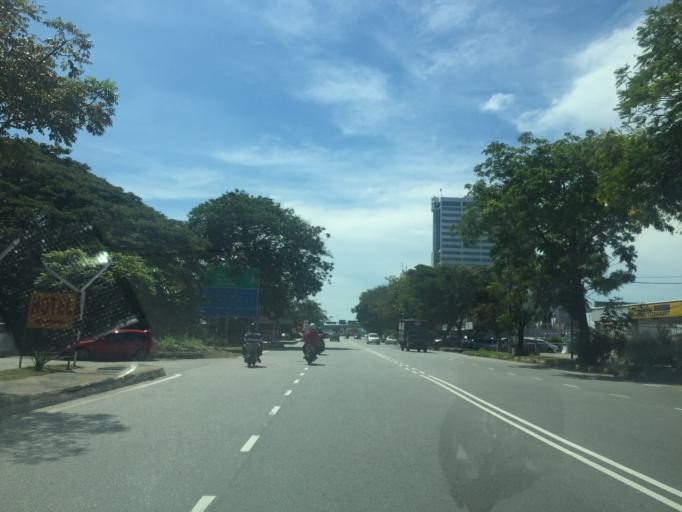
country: MY
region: Penang
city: Butterworth
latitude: 5.3993
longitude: 100.3681
